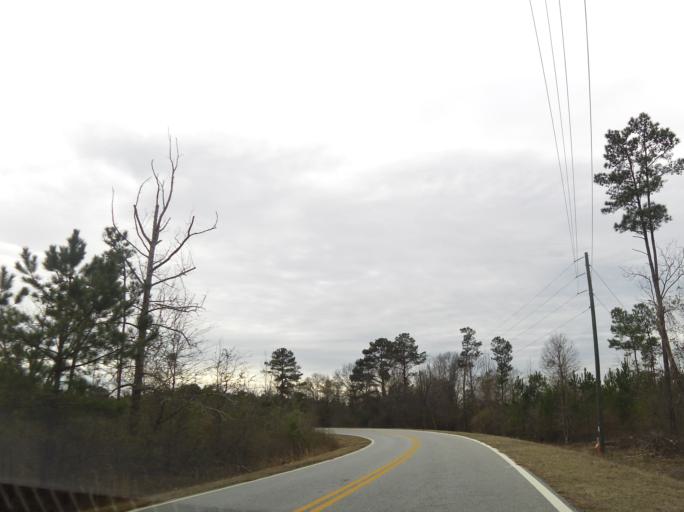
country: US
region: Georgia
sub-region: Bibb County
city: West Point
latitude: 32.8221
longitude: -83.7351
